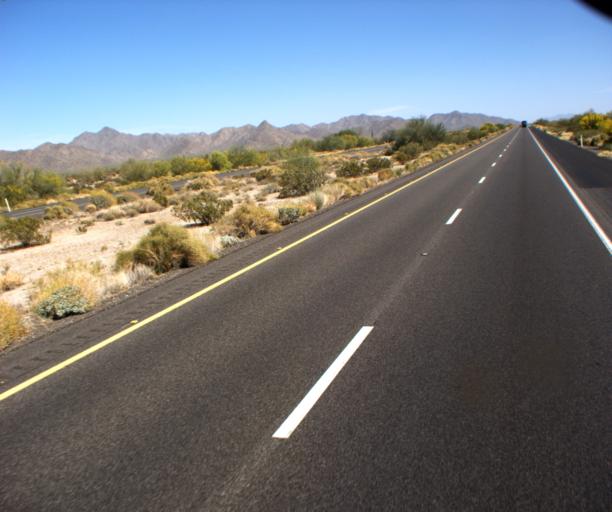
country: US
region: Arizona
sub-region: Maricopa County
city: Gila Bend
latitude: 32.8910
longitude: -112.4860
